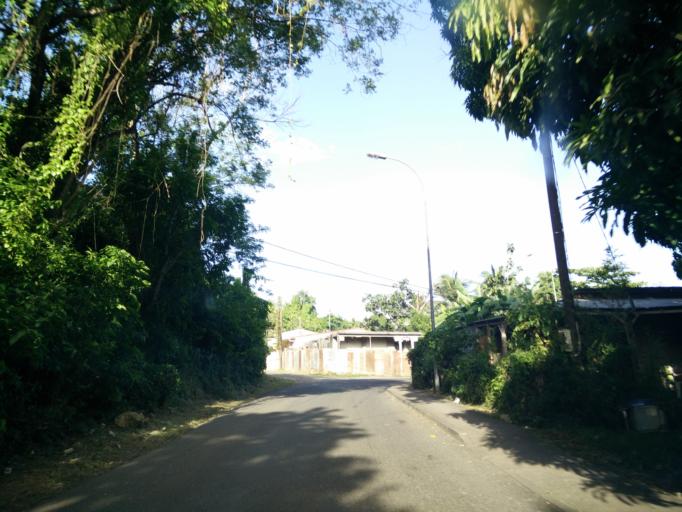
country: GP
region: Guadeloupe
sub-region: Guadeloupe
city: Les Abymes
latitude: 16.2518
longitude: -61.5138
